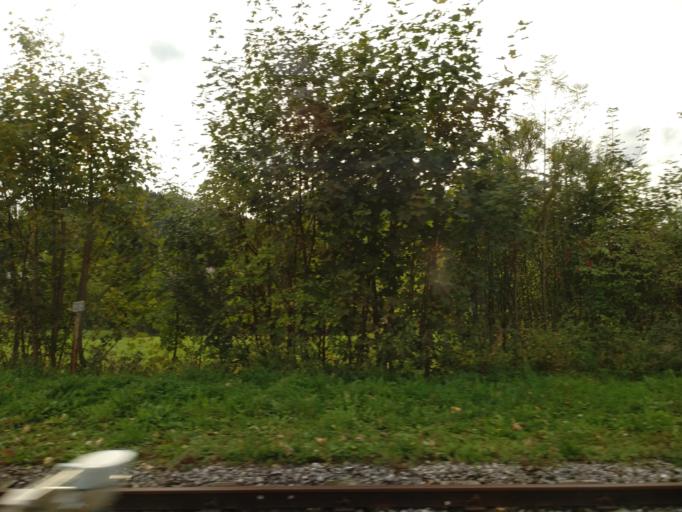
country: AT
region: Lower Austria
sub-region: Politischer Bezirk Lilienfeld
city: Mitterbach am Erlaufsee
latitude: 47.8661
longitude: 15.3107
